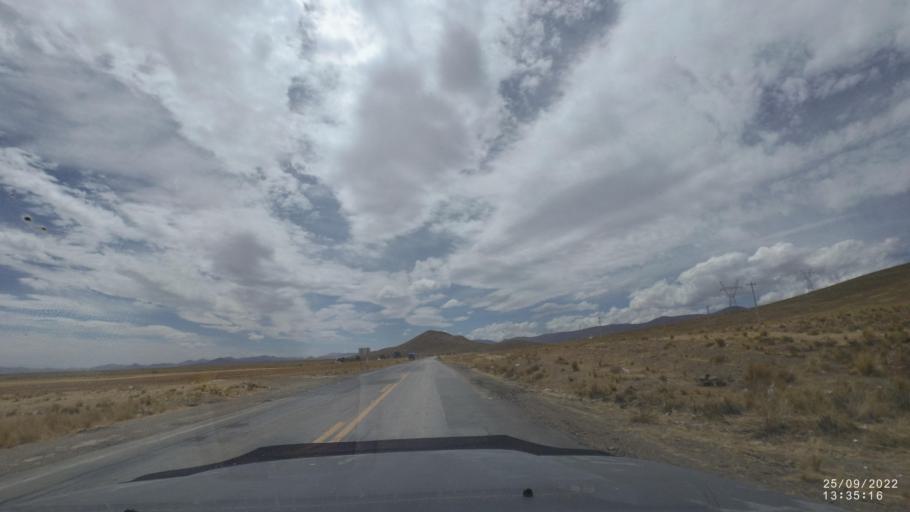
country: BO
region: Oruro
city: Oruro
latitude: -17.7251
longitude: -67.0475
